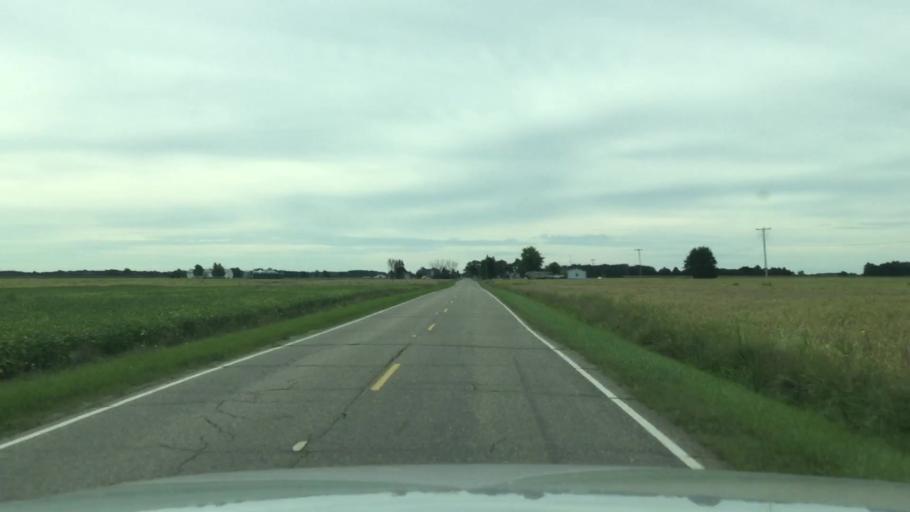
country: US
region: Michigan
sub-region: Genesee County
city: Montrose
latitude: 43.0948
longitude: -83.9878
